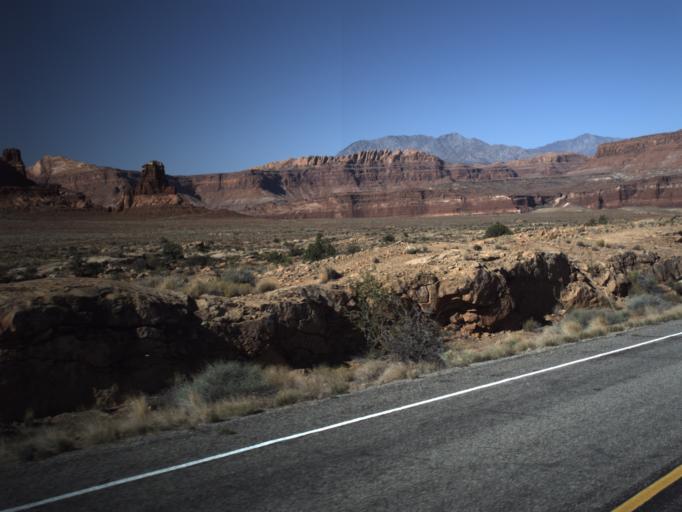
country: US
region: Utah
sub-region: San Juan County
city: Blanding
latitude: 37.8811
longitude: -110.3563
